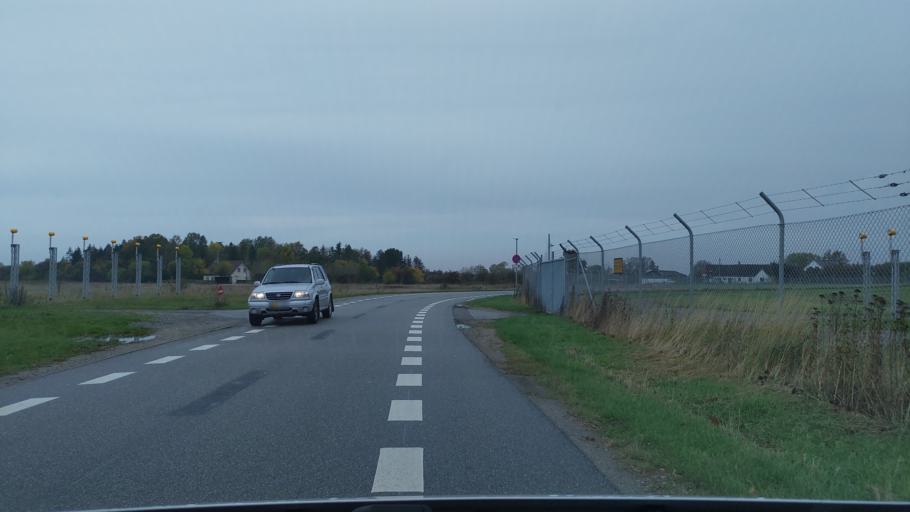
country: DK
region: Capital Region
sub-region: Tarnby Kommune
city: Tarnby
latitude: 55.5880
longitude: 12.5977
